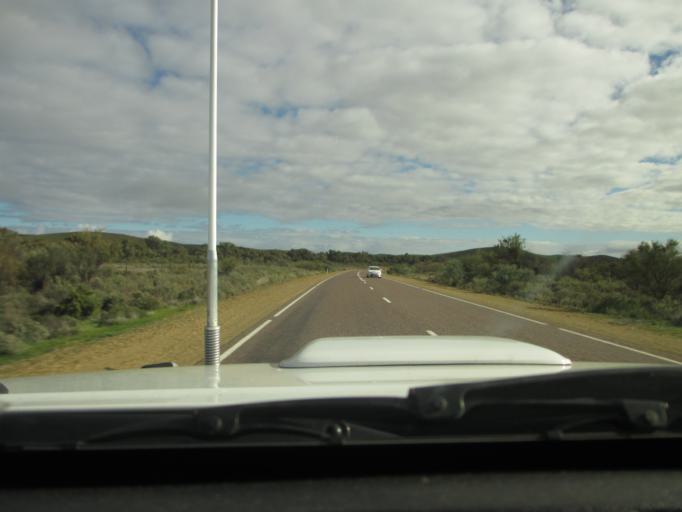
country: AU
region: South Australia
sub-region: Flinders Ranges
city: Quorn
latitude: -32.3363
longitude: 138.4761
